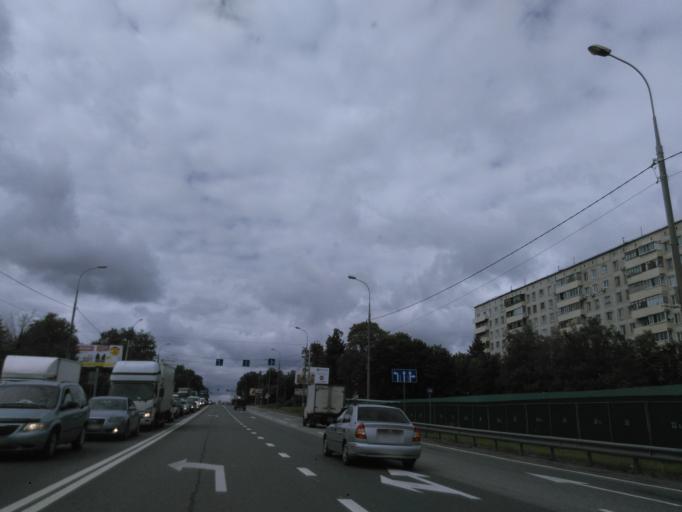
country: RU
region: Moskovskaya
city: Solnechnogorsk
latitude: 56.1983
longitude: 36.9605
